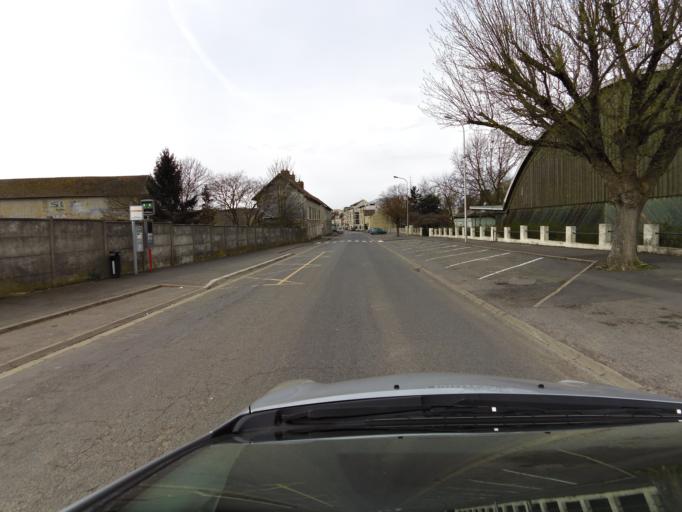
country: FR
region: Ile-de-France
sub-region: Departement de Seine-et-Marne
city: Villeparisis
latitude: 48.9405
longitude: 2.6209
